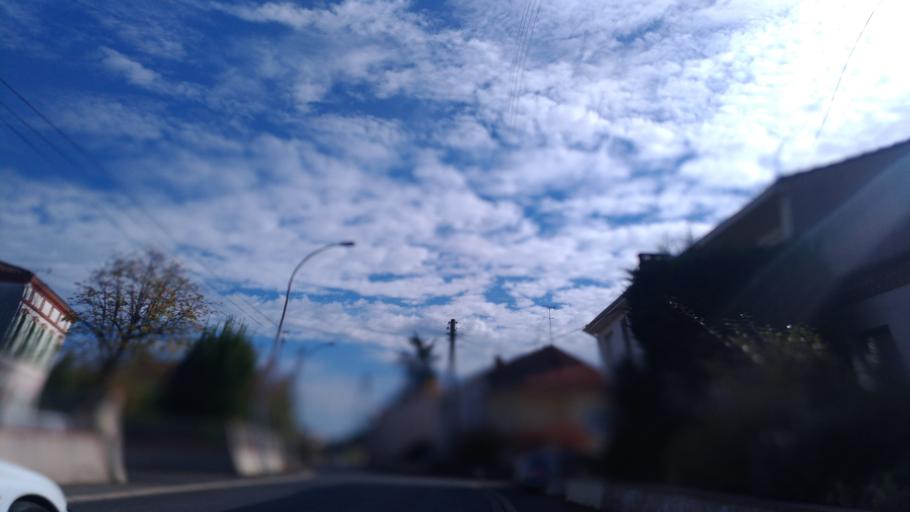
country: FR
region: Midi-Pyrenees
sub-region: Departement du Tarn
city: Albi
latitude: 43.9245
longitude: 2.1340
